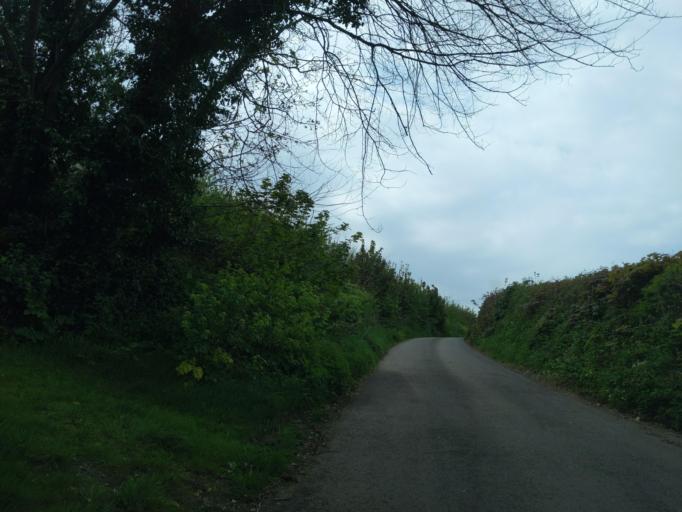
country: GB
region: England
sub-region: Borough of Torbay
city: Brixham
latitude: 50.3886
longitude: -3.5532
